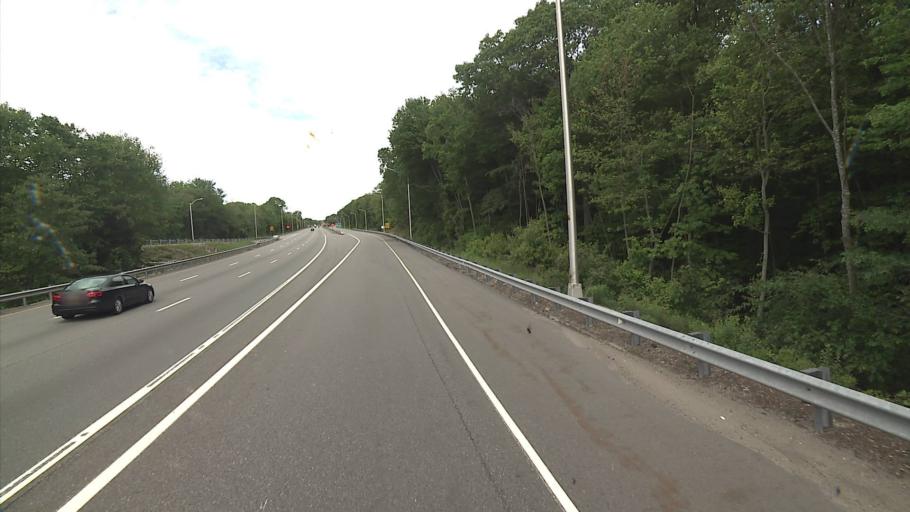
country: US
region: Connecticut
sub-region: New London County
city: Long Hill
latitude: 41.3622
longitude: -72.0572
